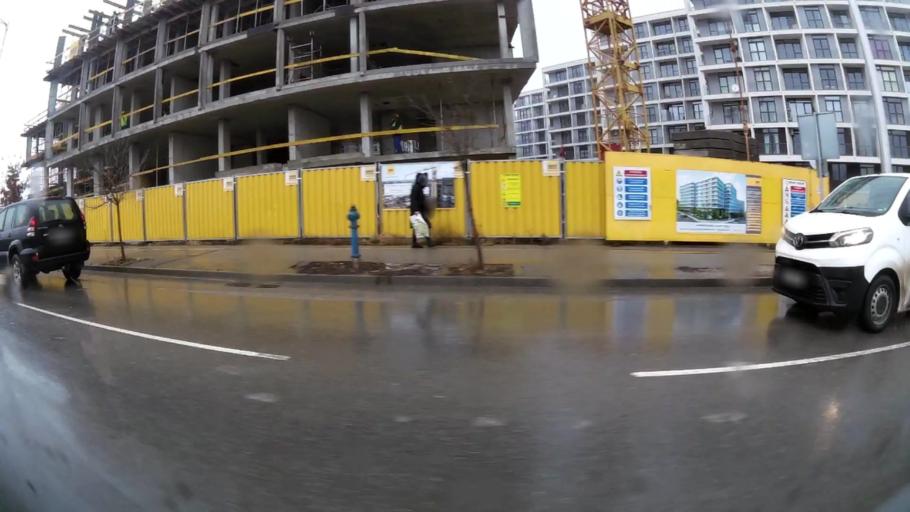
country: BG
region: Sofia-Capital
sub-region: Stolichna Obshtina
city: Sofia
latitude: 42.6447
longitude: 23.4017
